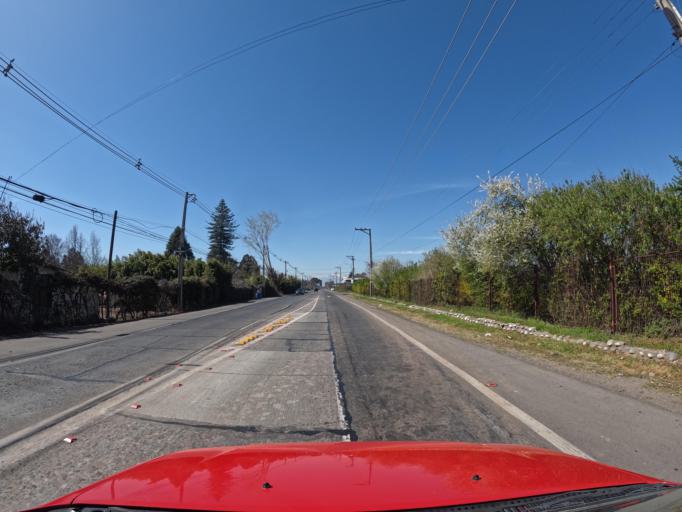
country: CL
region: Maule
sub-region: Provincia de Curico
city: Curico
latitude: -34.9644
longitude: -71.1889
